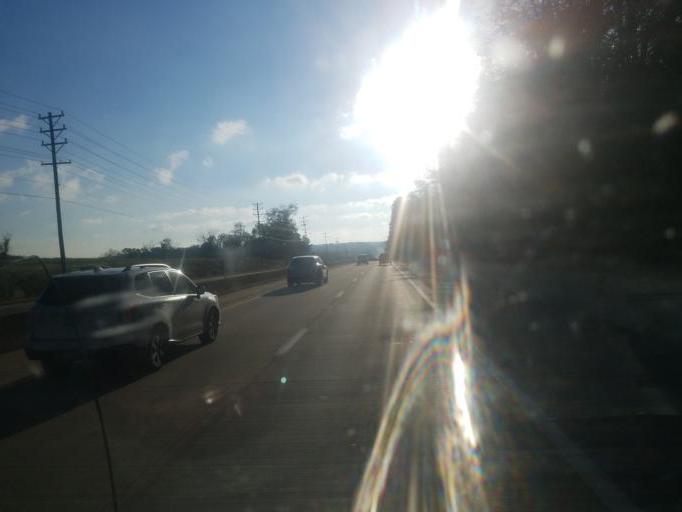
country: US
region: Pennsylvania
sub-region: Westmoreland County
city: Delmont
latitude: 40.4108
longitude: -79.6215
